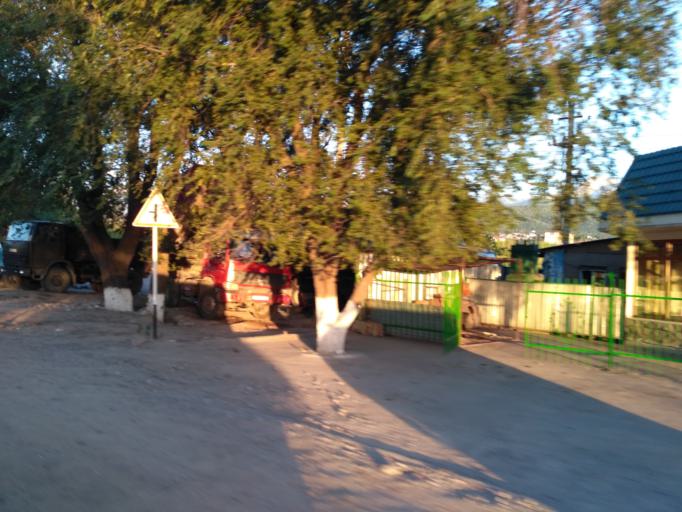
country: KZ
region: Almaty Qalasy
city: Almaty
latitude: 43.1747
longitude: 76.7876
